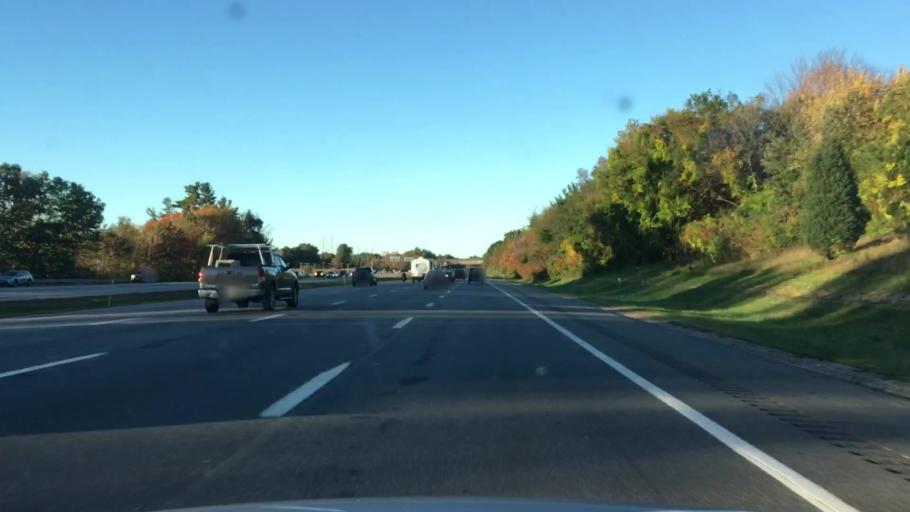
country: US
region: New Hampshire
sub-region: Rockingham County
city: North Hampton
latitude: 42.9768
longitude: -70.8531
